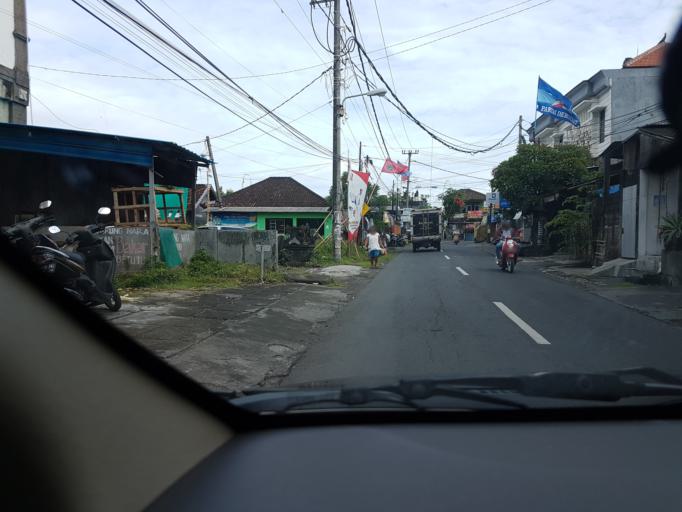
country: ID
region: Bali
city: Denpasar
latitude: -8.6673
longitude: 115.1917
